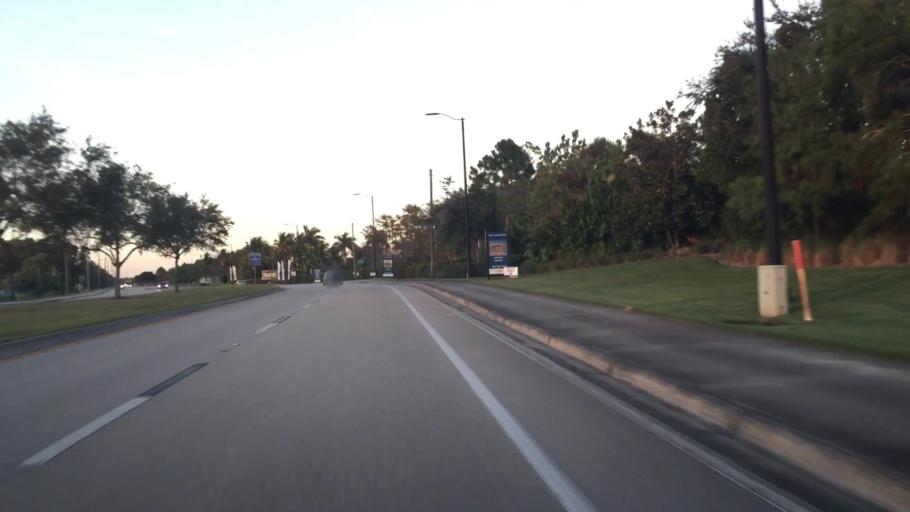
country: US
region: Florida
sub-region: Lee County
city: Gateway
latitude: 26.5536
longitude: -81.7865
